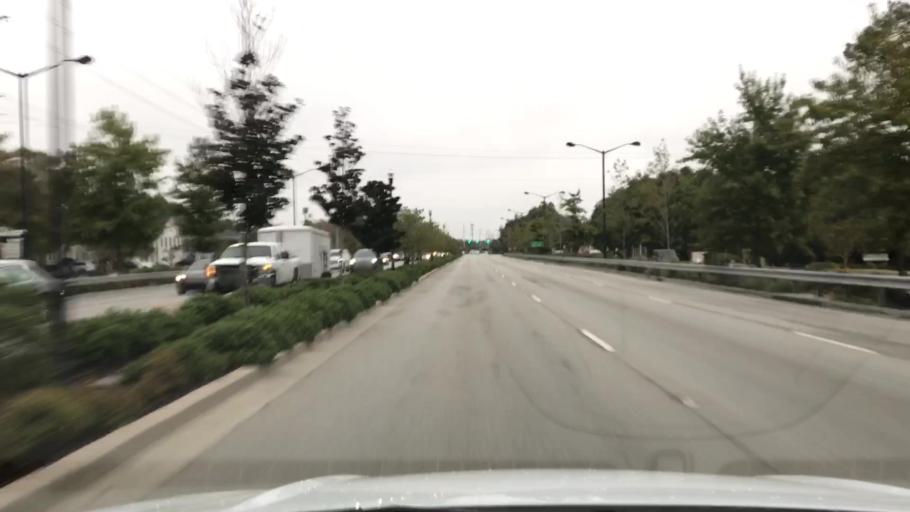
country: US
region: South Carolina
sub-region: Charleston County
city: Mount Pleasant
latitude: 32.8094
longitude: -79.8741
